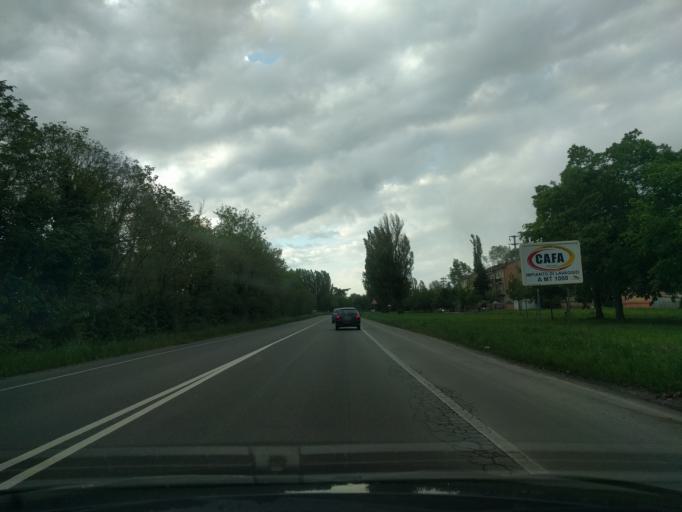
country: IT
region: Emilia-Romagna
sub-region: Provincia di Ferrara
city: Ferrara
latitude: 44.8648
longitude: 11.6020
